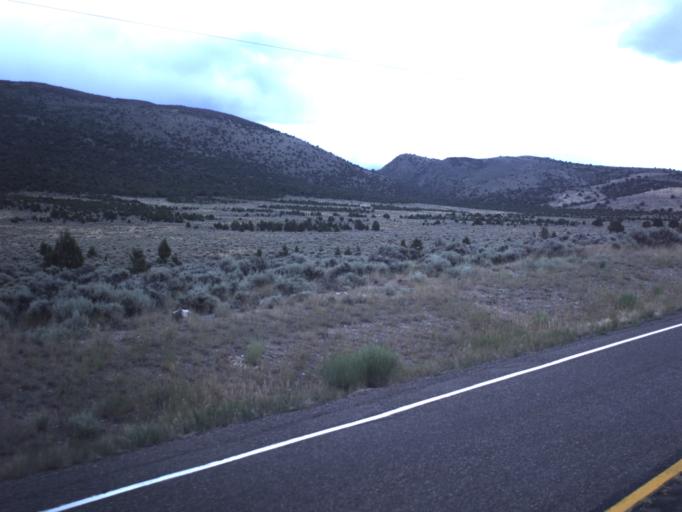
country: US
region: Utah
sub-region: Wayne County
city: Loa
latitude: 38.5532
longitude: -111.8363
